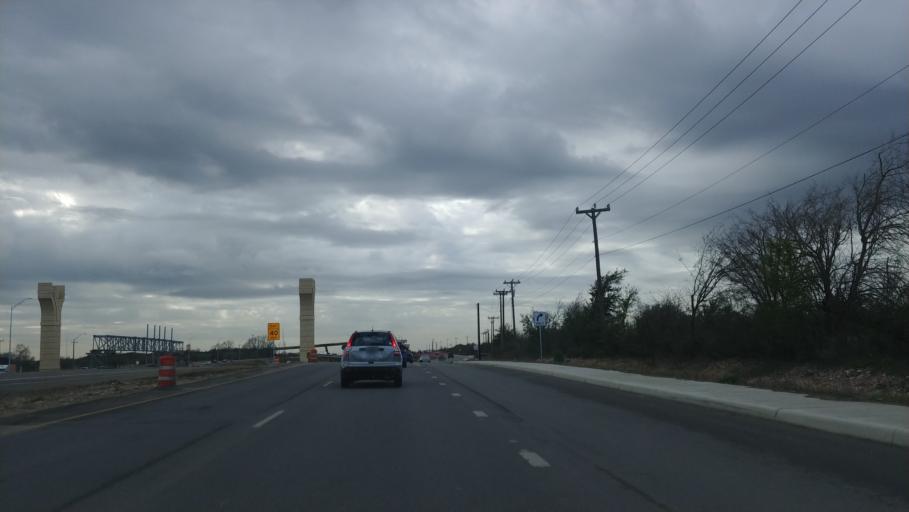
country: US
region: Texas
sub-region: Bexar County
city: Lackland Air Force Base
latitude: 29.3936
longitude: -98.7029
